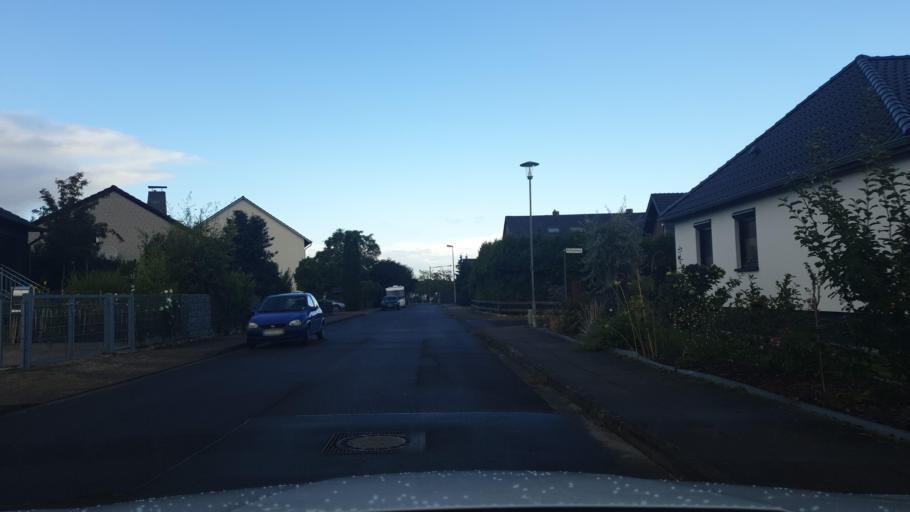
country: DE
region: North Rhine-Westphalia
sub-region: Regierungsbezirk Detmold
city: Petershagen
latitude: 52.3748
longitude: 8.9564
